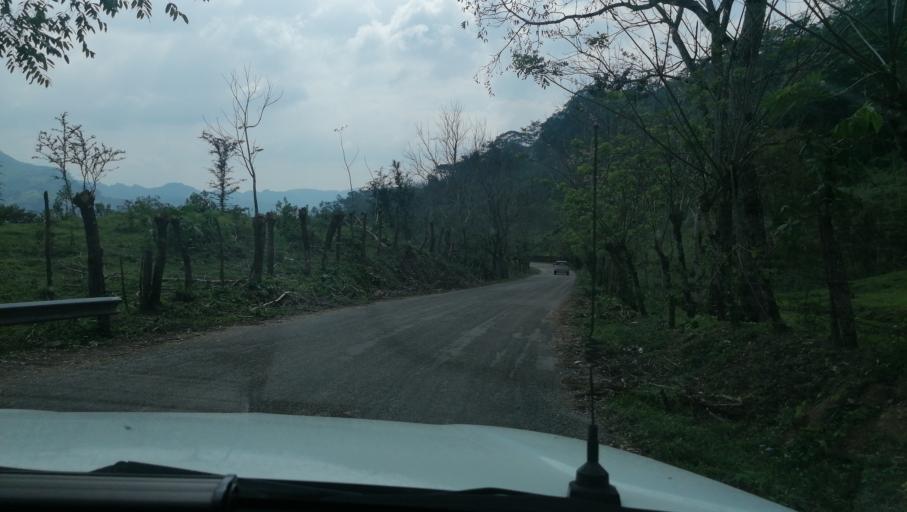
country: MX
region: Chiapas
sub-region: Francisco Leon
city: San Miguel la Sardina
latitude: 17.2286
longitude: -93.3419
